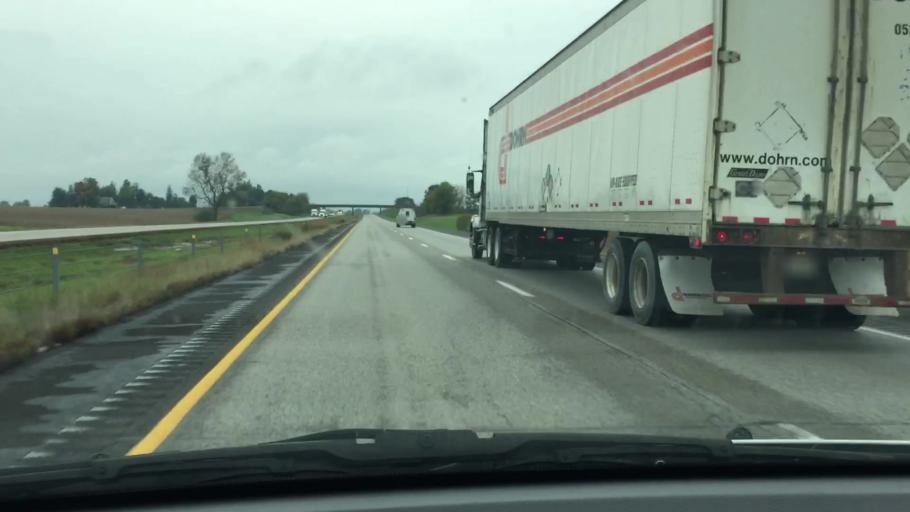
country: US
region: Iowa
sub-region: Johnson County
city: Tiffin
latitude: 41.6934
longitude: -91.7477
